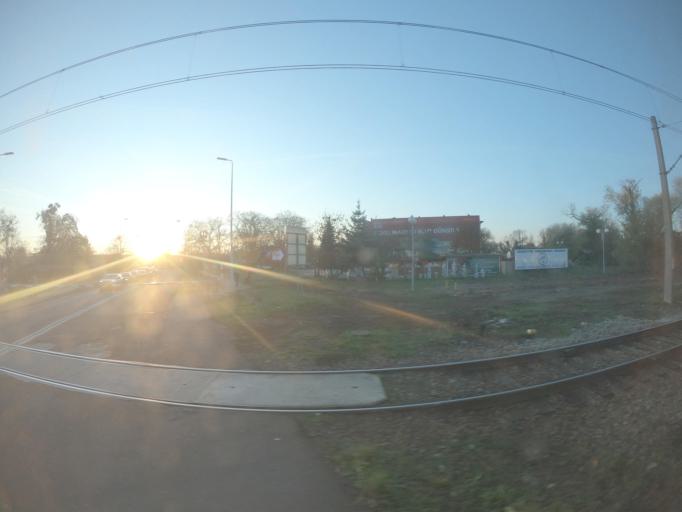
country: PL
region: Lubusz
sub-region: Powiat gorzowski
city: Kostrzyn nad Odra
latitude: 52.5812
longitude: 14.6427
